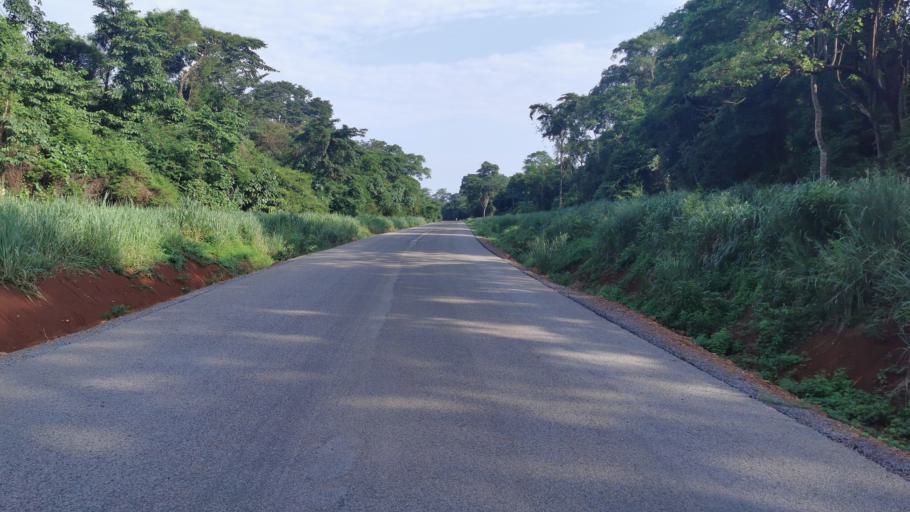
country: ET
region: Gambela
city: Gambela
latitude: 7.7177
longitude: 34.6615
